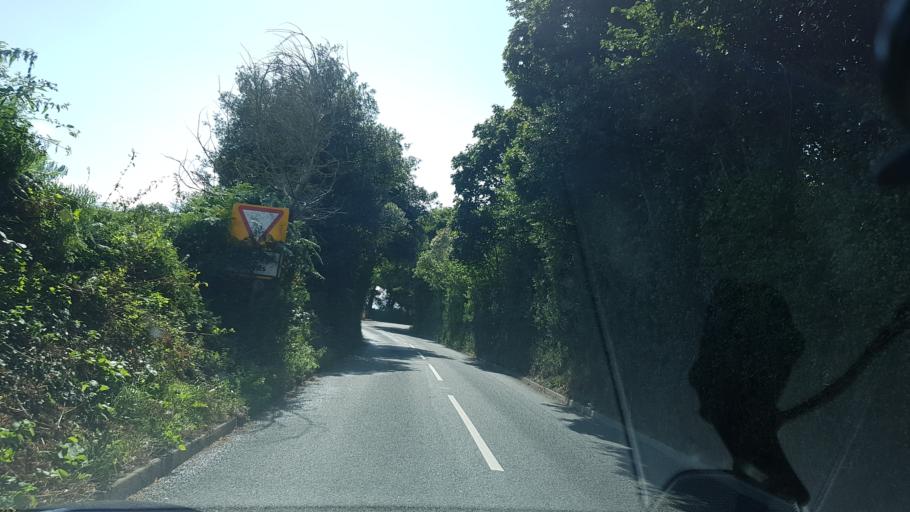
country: GB
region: England
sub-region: Surrey
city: West Byfleet
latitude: 51.3196
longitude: -0.5106
